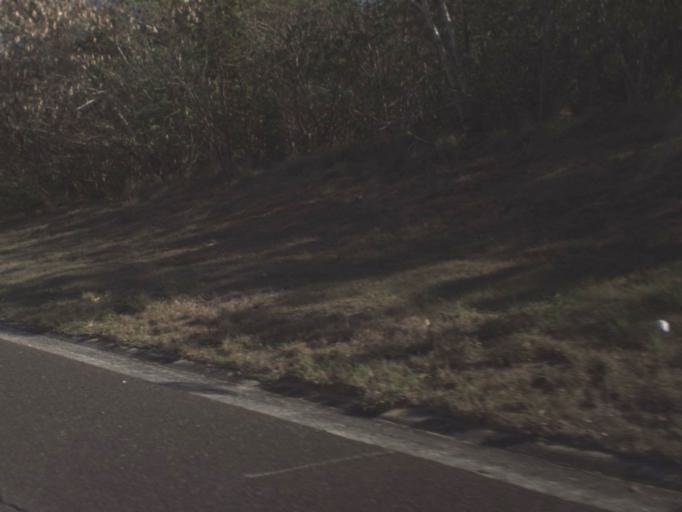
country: US
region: Florida
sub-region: Lake County
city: Minneola
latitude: 28.6092
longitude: -81.7578
